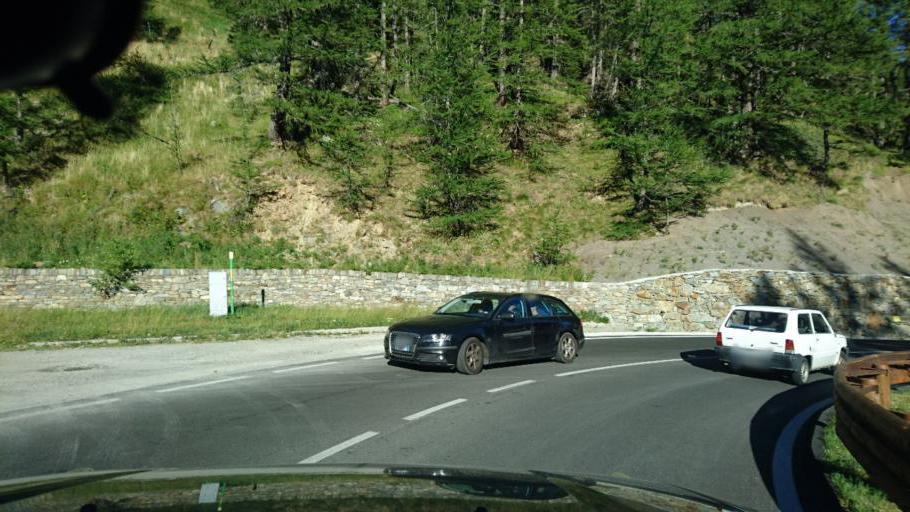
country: IT
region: Aosta Valley
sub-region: Valle d'Aosta
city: San Leonardo
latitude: 45.8457
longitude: 7.1755
